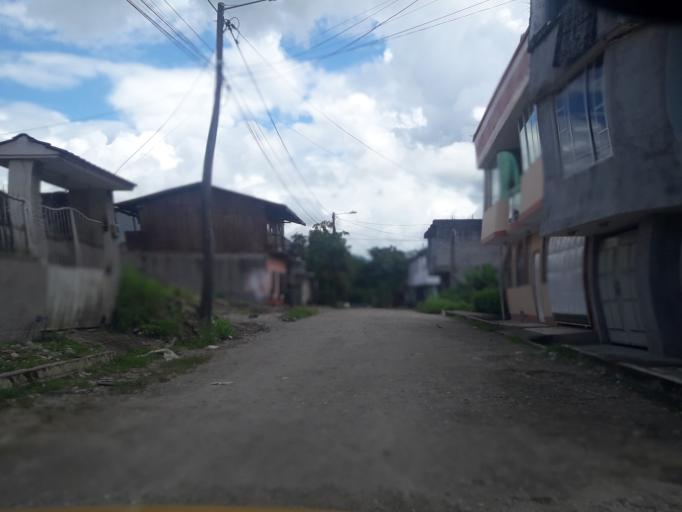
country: EC
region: Napo
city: Tena
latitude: -1.0032
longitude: -77.8169
